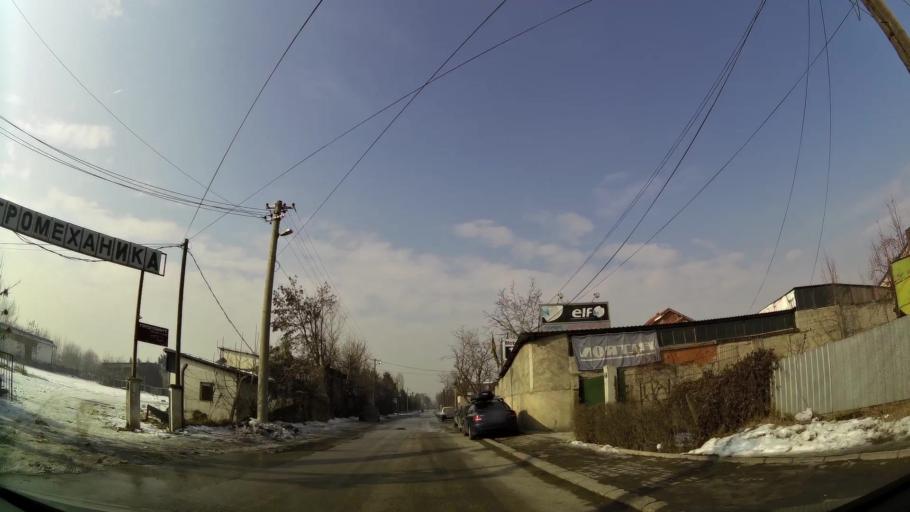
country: MK
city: Krushopek
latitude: 42.0145
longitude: 21.3820
